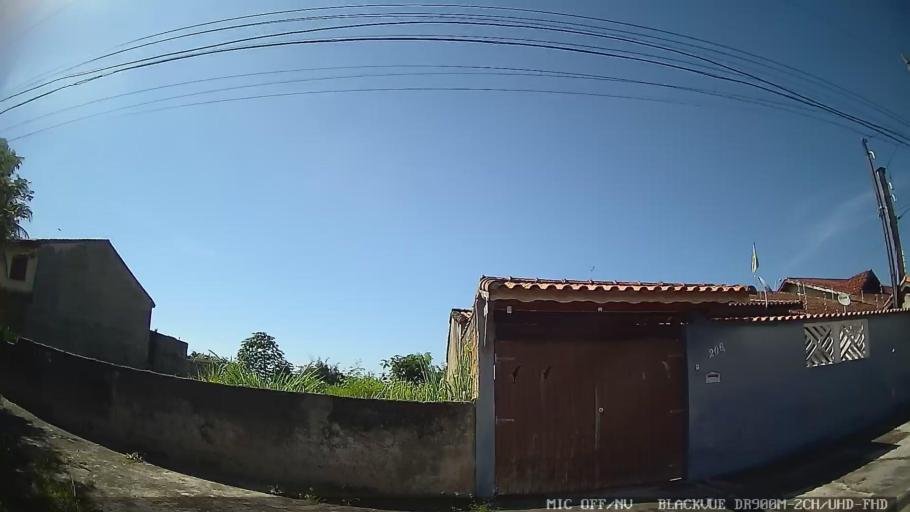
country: BR
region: Sao Paulo
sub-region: Peruibe
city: Peruibe
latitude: -24.2705
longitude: -46.9387
